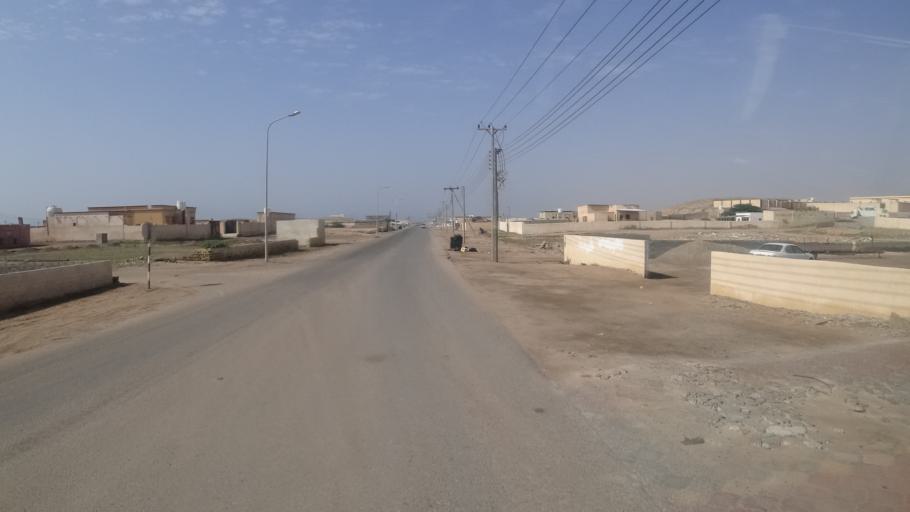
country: OM
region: Ash Sharqiyah
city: Sur
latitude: 22.1767
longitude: 59.7612
